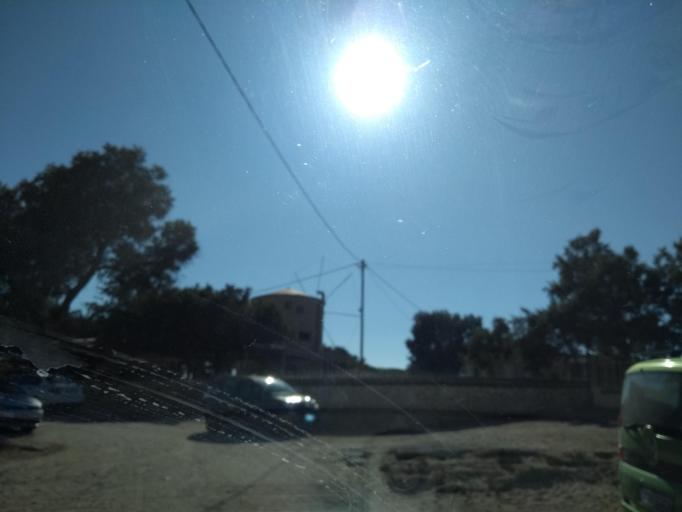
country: GR
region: Crete
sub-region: Nomos Chanias
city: Pithari
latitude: 35.5927
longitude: 24.0954
